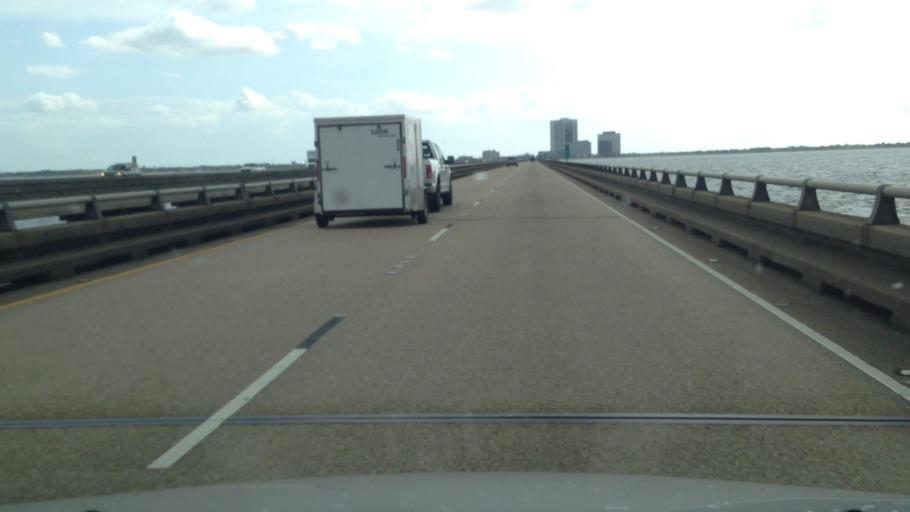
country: US
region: Louisiana
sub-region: Jefferson Parish
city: Metairie
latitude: 30.0442
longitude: -90.1502
